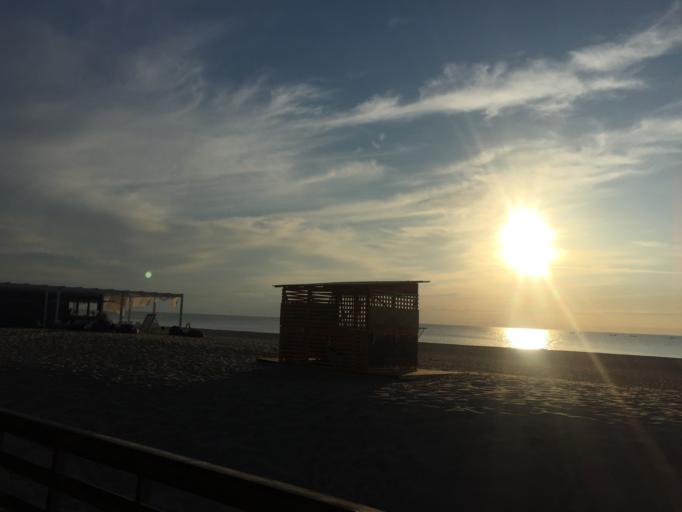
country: RU
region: Kaliningrad
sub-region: Gorod Kaliningrad
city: Yantarnyy
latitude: 54.8694
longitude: 19.9335
